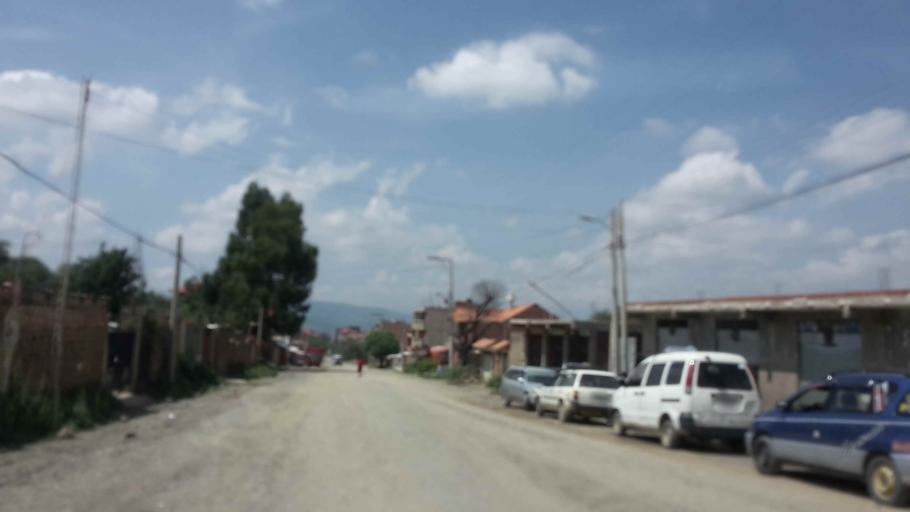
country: BO
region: Cochabamba
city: Cochabamba
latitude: -17.3302
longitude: -66.2186
